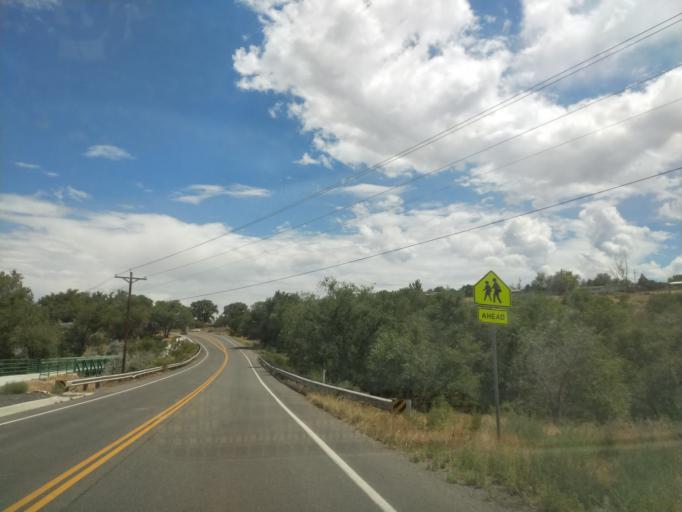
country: US
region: Colorado
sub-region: Mesa County
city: Redlands
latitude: 39.0707
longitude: -108.6174
